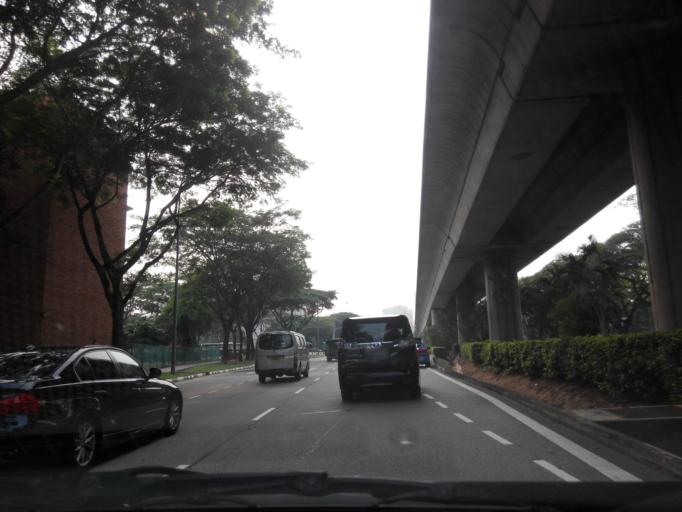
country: SG
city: Singapore
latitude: 1.3011
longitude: 103.7997
